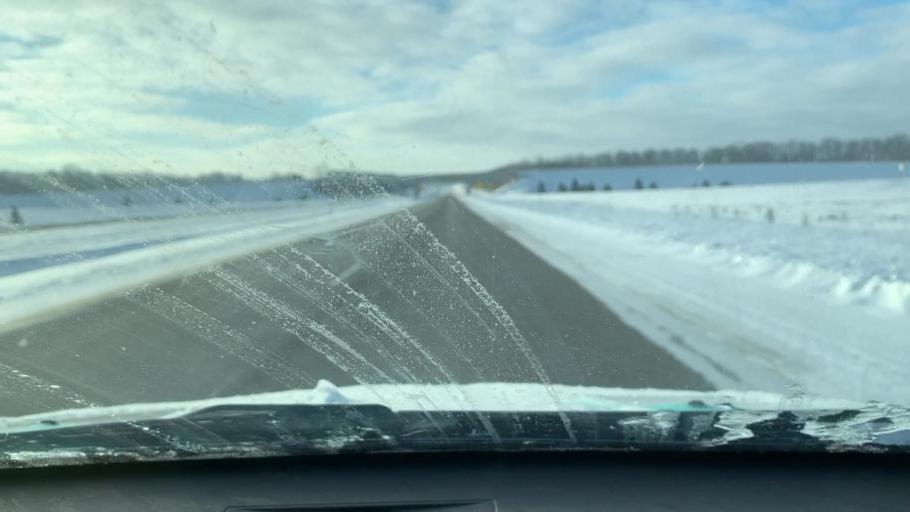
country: US
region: Michigan
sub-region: Wexford County
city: Cadillac
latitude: 44.2860
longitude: -85.3888
